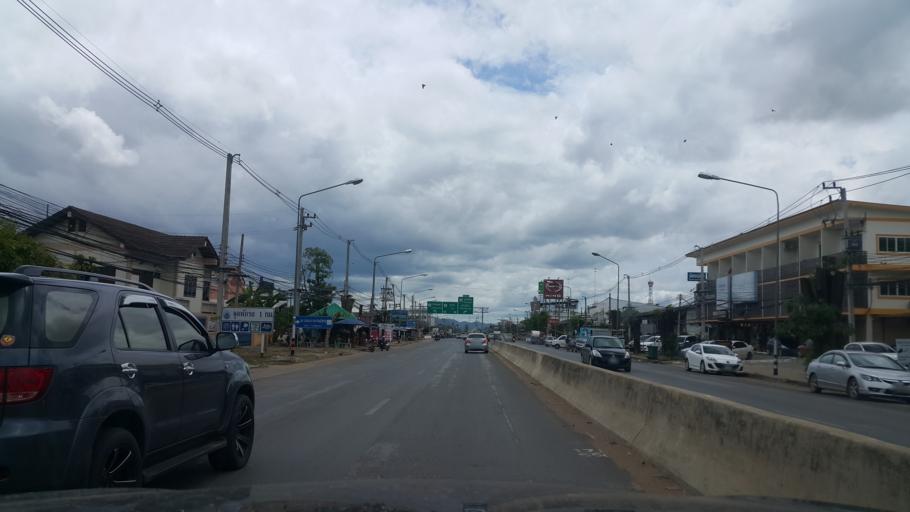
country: TH
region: Sukhothai
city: Sukhothai
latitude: 17.0089
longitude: 99.8088
